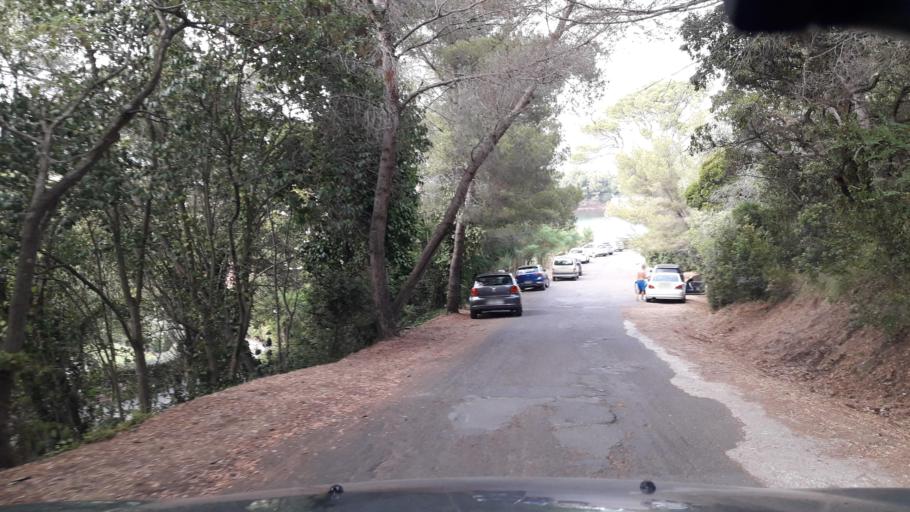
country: FR
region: Provence-Alpes-Cote d'Azur
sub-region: Departement du Var
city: Saint-Raphael
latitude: 43.4188
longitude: 6.8563
